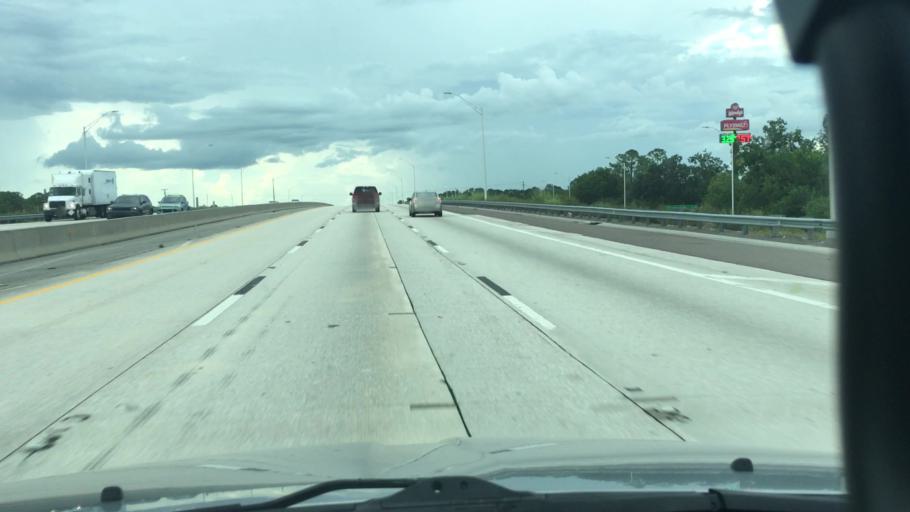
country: US
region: Florida
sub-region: Brevard County
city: Cocoa West
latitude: 28.3725
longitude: -80.8028
